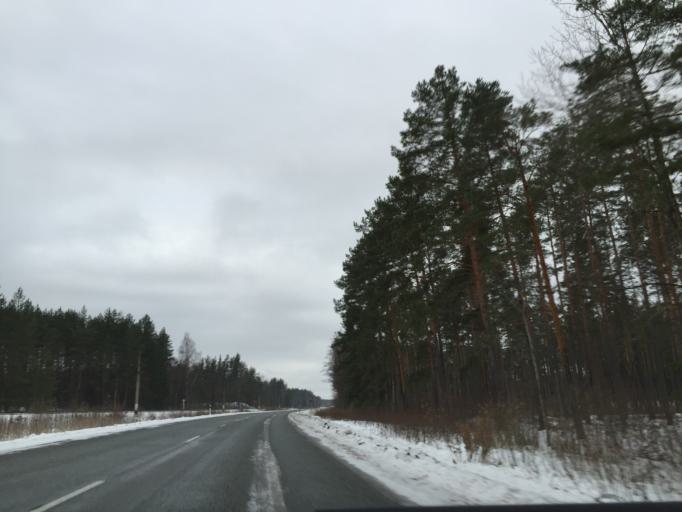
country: LV
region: Saulkrastu
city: Saulkrasti
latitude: 57.2079
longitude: 24.3798
